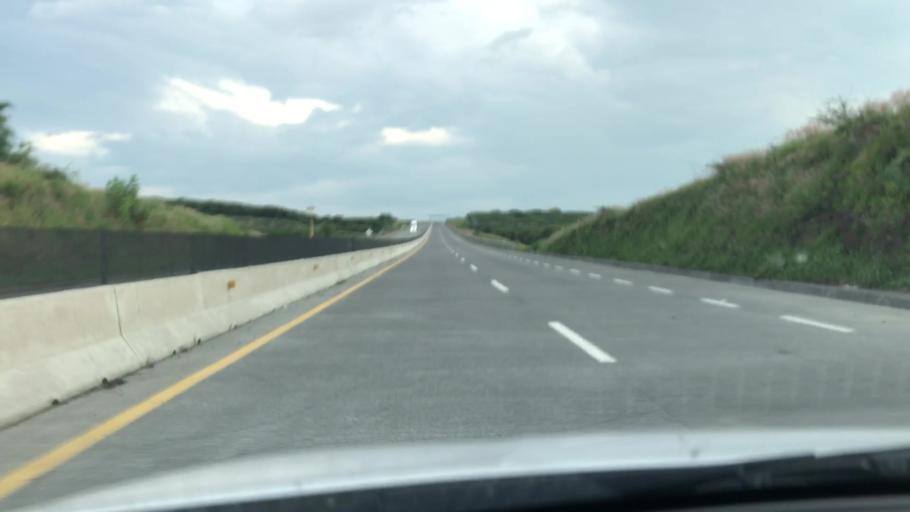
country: MX
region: Jalisco
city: Degollado
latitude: 20.3768
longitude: -102.1230
